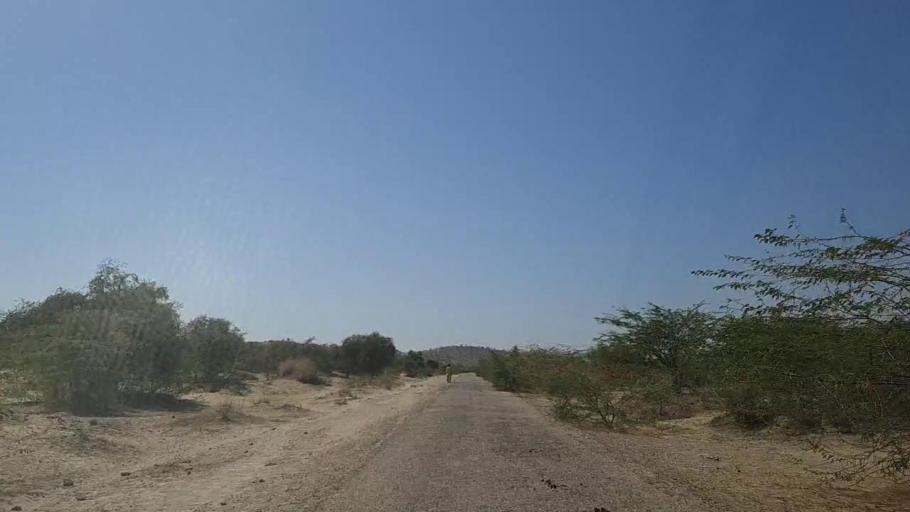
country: PK
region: Sindh
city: Mithi
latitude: 24.8013
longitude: 69.7176
